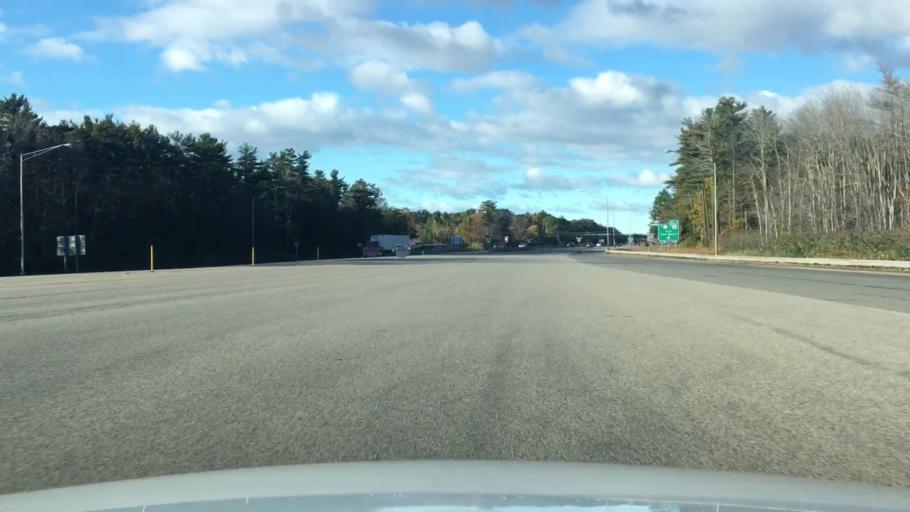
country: US
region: Maine
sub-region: York County
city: York Harbor
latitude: 43.1596
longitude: -70.6603
